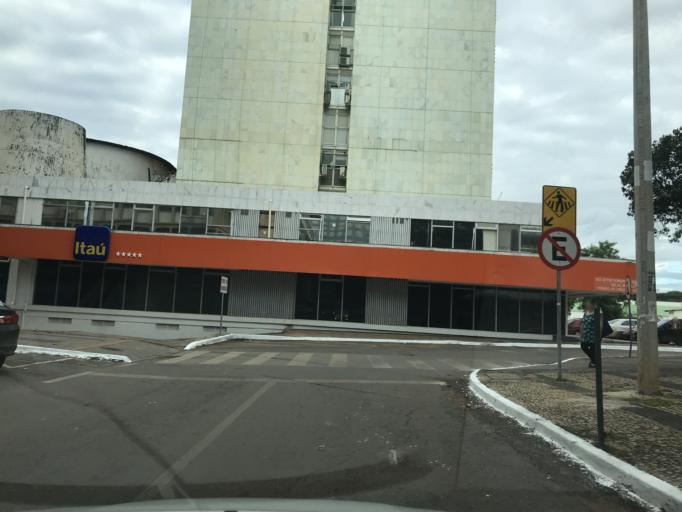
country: BR
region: Federal District
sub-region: Brasilia
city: Brasilia
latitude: -15.7986
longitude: -47.8878
